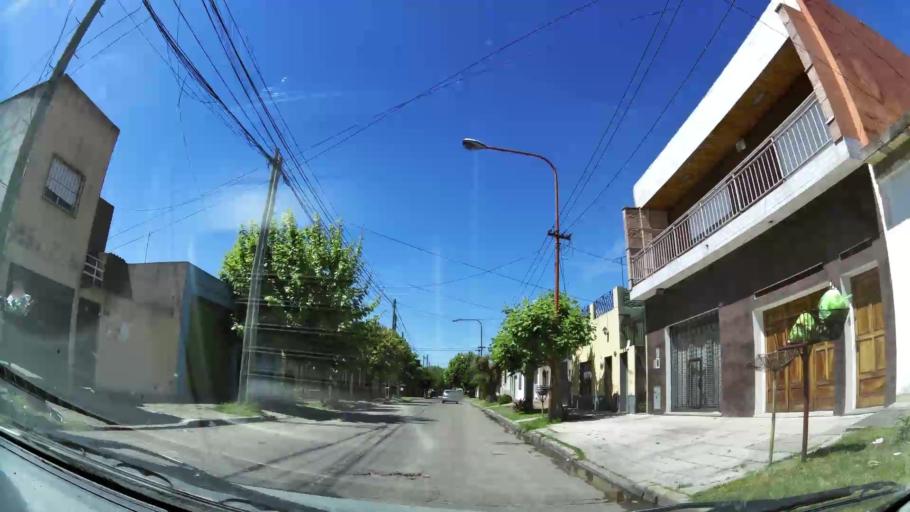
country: AR
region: Buenos Aires
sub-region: Partido de Quilmes
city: Quilmes
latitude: -34.7258
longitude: -58.2783
